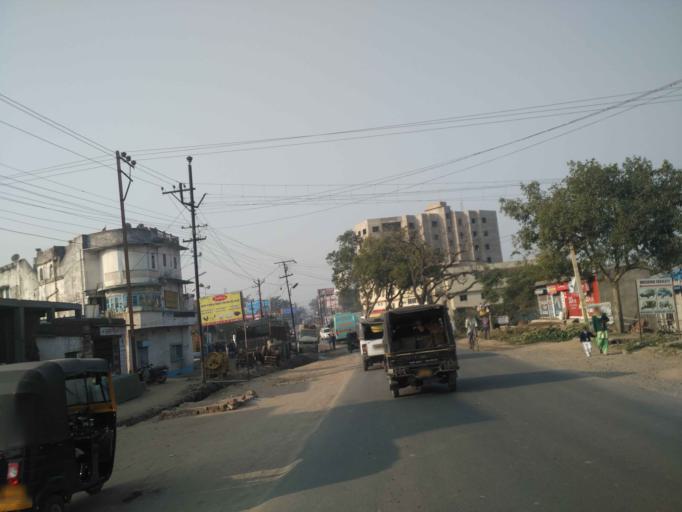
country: IN
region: Jharkhand
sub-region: Ranchi
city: Ranchi
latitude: 23.3794
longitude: 85.3624
